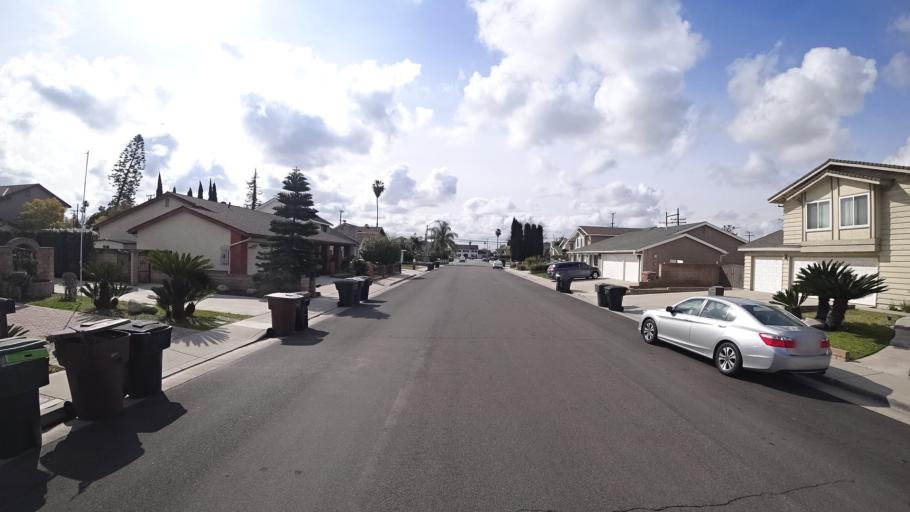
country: US
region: California
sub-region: Orange County
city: Stanton
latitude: 33.8258
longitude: -117.9629
